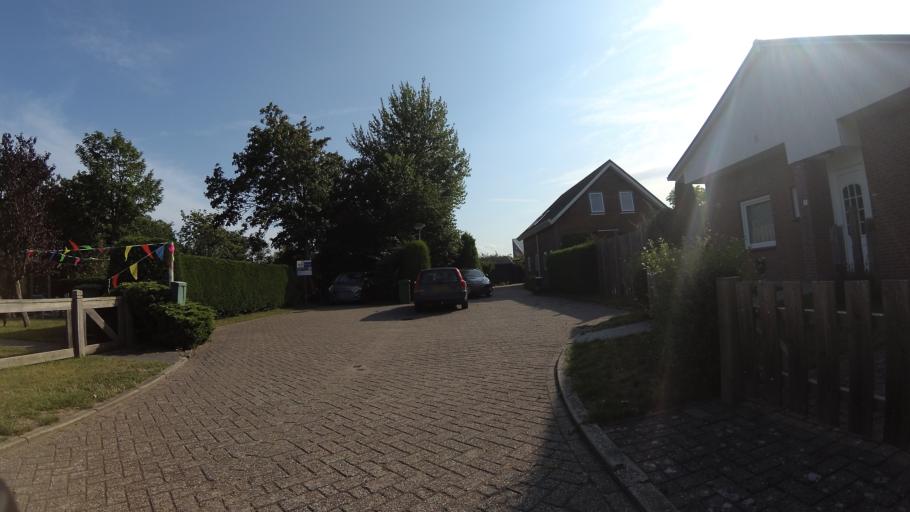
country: NL
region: Zeeland
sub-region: Gemeente Veere
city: Veere
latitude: 51.5675
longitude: 3.6686
